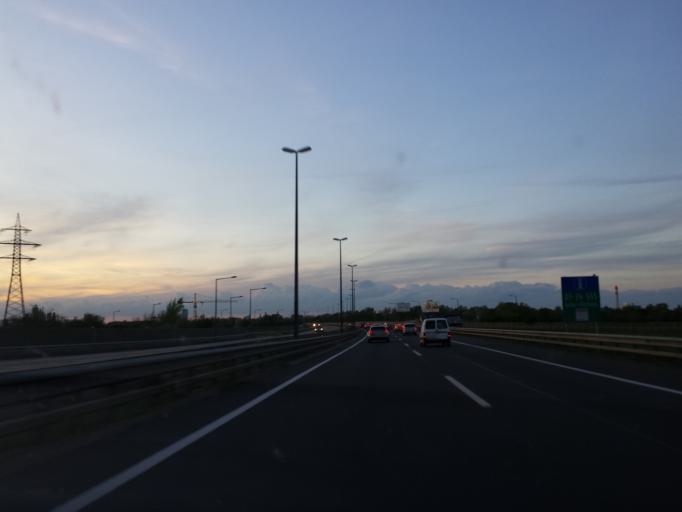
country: AT
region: Lower Austria
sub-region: Politischer Bezirk Wien-Umgebung
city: Schwechat
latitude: 48.1731
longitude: 16.4552
